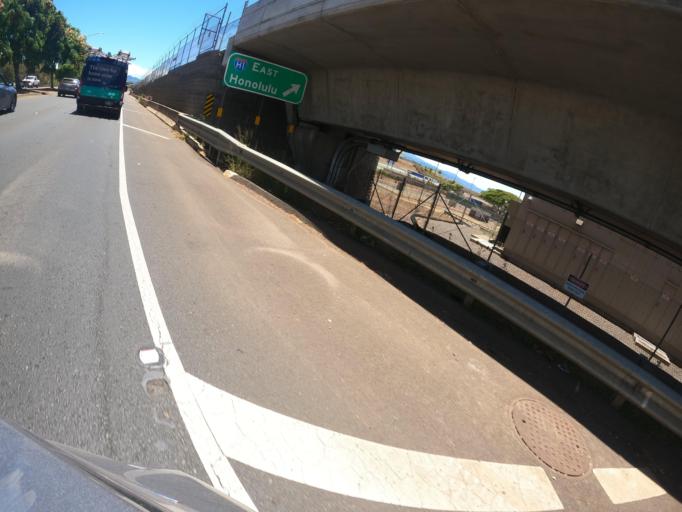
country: US
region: Hawaii
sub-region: Honolulu County
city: Waipahu
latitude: 21.3911
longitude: -157.9927
